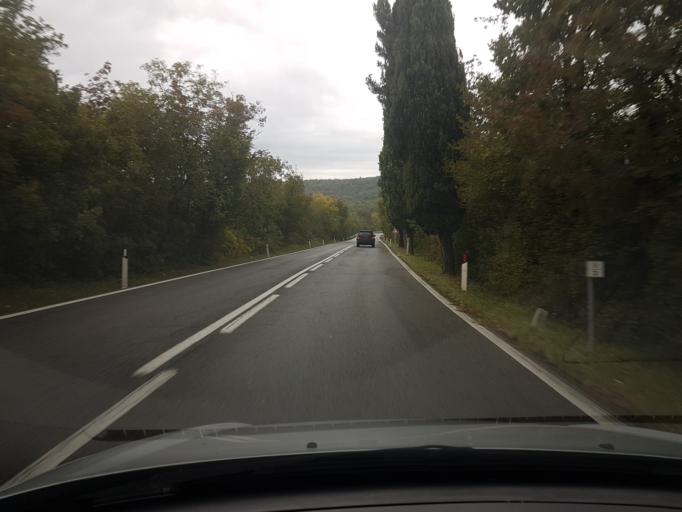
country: IT
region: Friuli Venezia Giulia
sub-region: Provincia di Gorizia
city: Monfalcone
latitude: 45.8127
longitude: 13.5752
